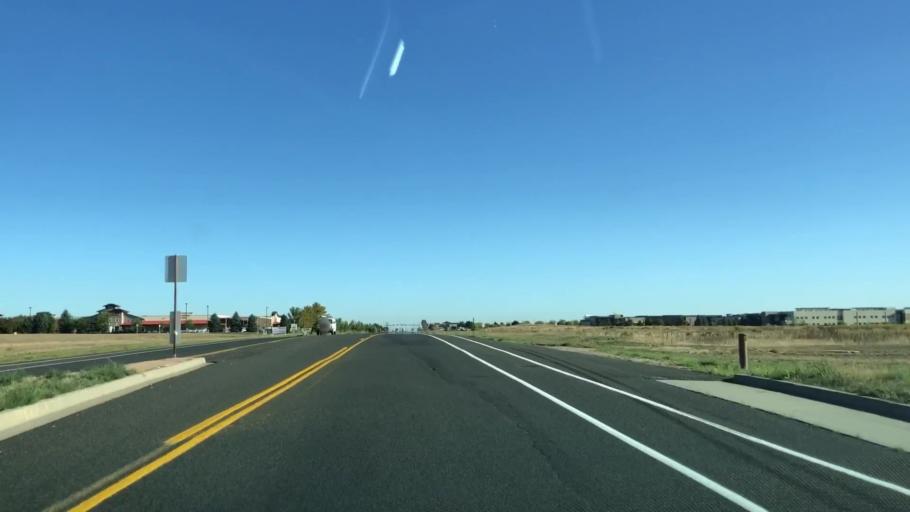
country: US
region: Colorado
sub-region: Weld County
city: Windsor
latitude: 40.4286
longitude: -104.9827
